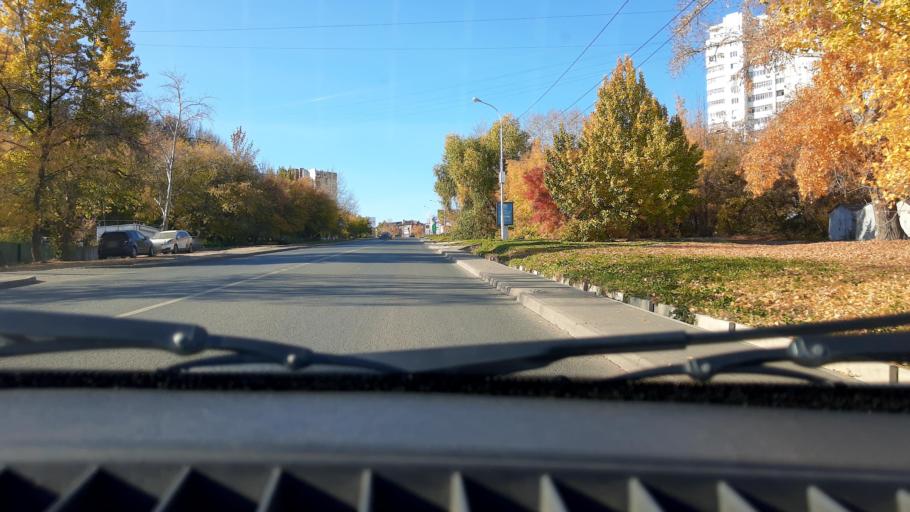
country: RU
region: Bashkortostan
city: Ufa
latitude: 54.7829
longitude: 56.0424
